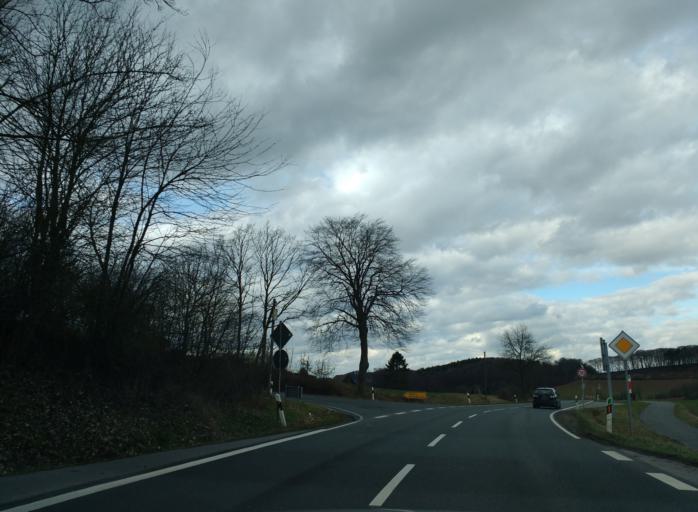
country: DE
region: North Rhine-Westphalia
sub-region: Regierungsbezirk Detmold
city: Lemgo
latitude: 52.0863
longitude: 8.9346
